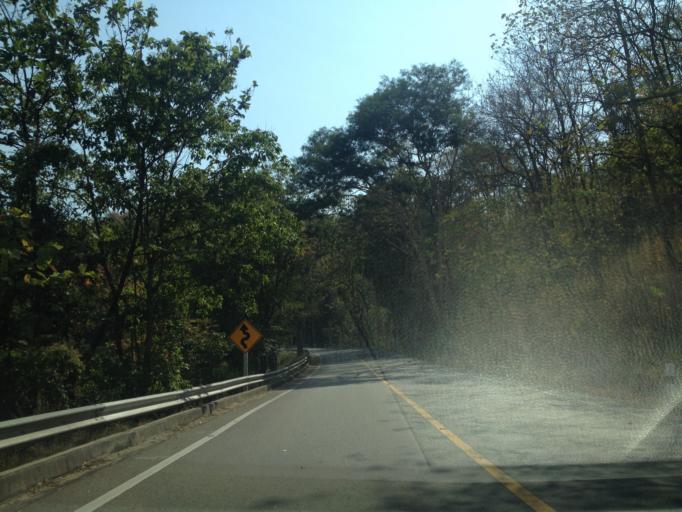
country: TH
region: Chiang Mai
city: Hot
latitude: 18.2076
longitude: 98.5895
